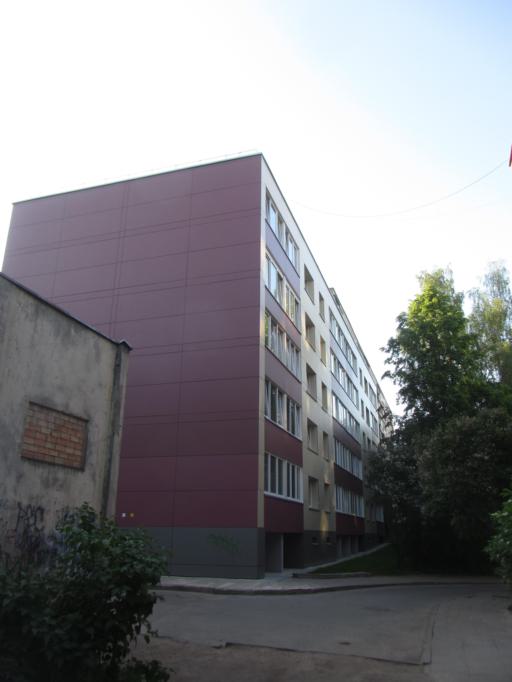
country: LT
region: Vilnius County
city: Seskine
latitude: 54.7276
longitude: 25.2716
